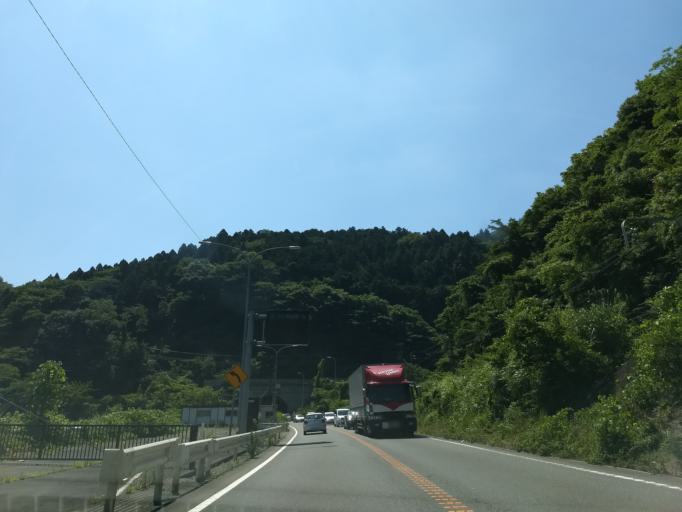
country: JP
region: Shizuoka
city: Gotemba
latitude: 35.3640
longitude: 139.0403
